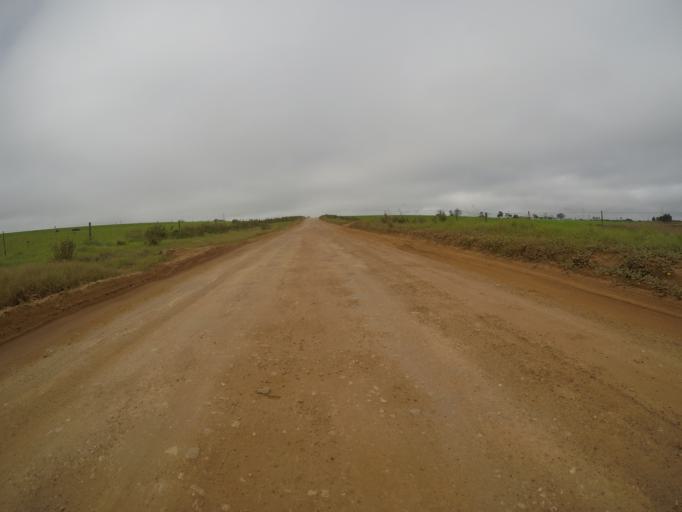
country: ZA
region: Eastern Cape
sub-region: Cacadu District Municipality
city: Kareedouw
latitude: -34.0283
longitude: 24.2429
